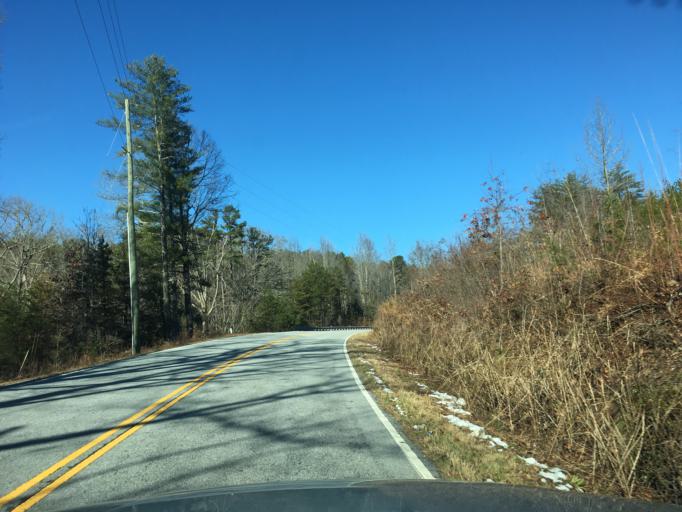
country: US
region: South Carolina
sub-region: Oconee County
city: Walhalla
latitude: 34.9154
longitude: -82.9853
